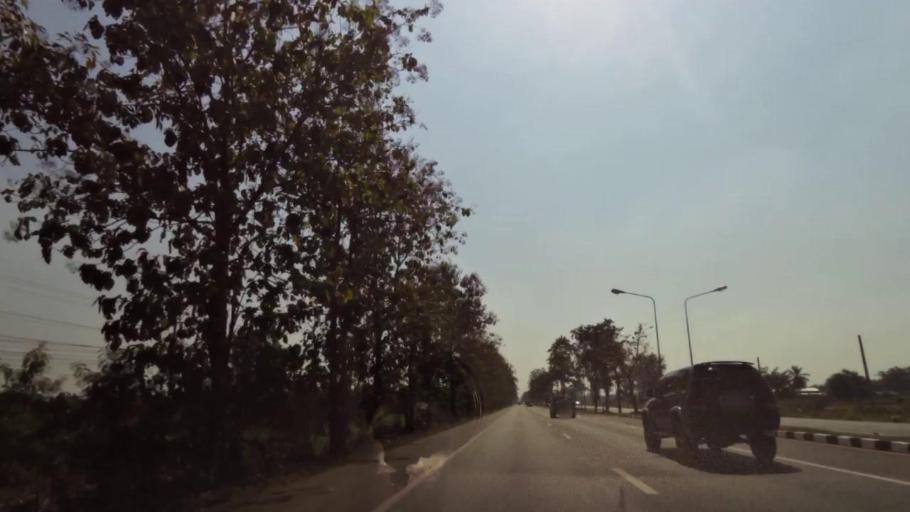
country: TH
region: Phichit
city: Bueng Na Rang
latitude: 16.0901
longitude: 100.1251
